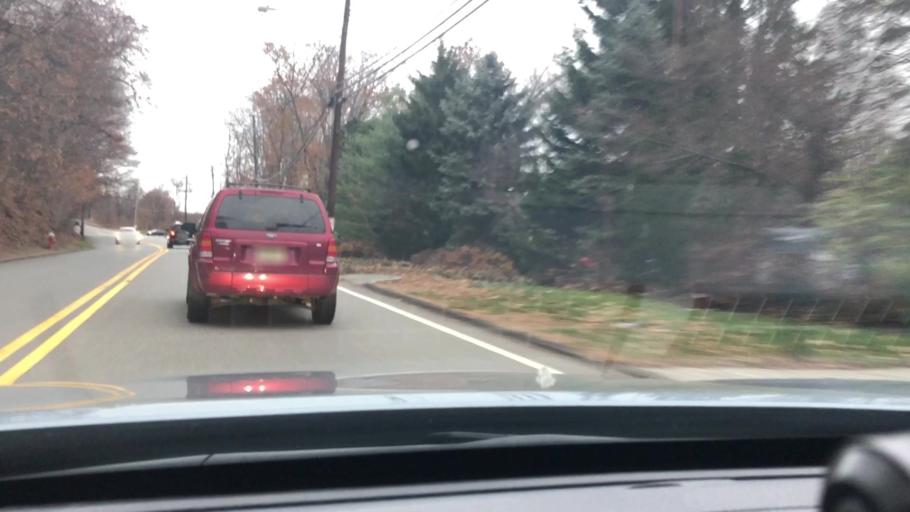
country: US
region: New Jersey
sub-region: Bergen County
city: Woodcliff Lake
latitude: 41.0103
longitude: -74.0699
